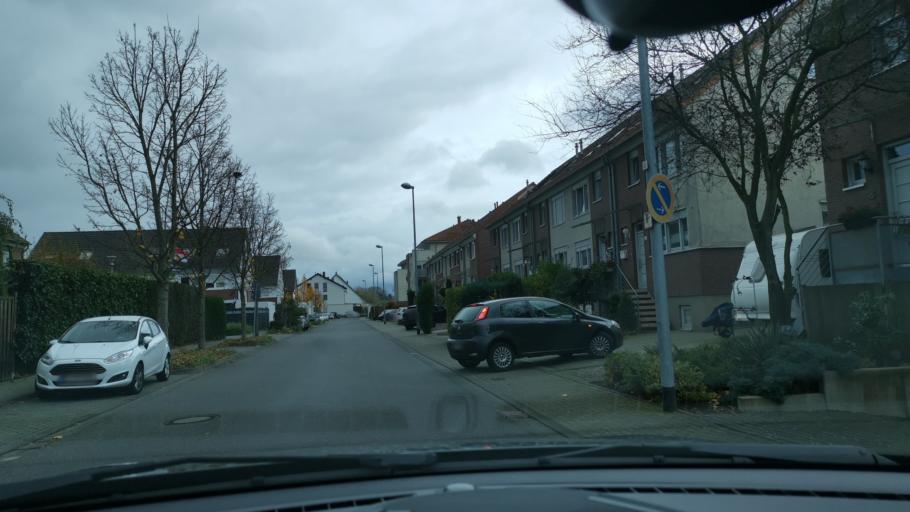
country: DE
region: North Rhine-Westphalia
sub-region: Regierungsbezirk Dusseldorf
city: Grevenbroich
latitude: 51.0896
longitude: 6.5978
